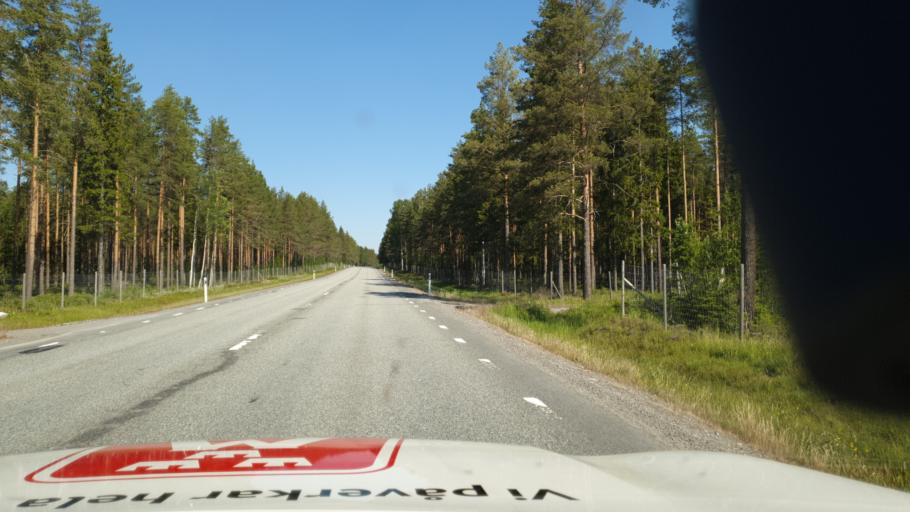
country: SE
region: Vaesterbotten
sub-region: Skelleftea Kommun
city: Burea
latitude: 64.5235
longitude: 21.2588
